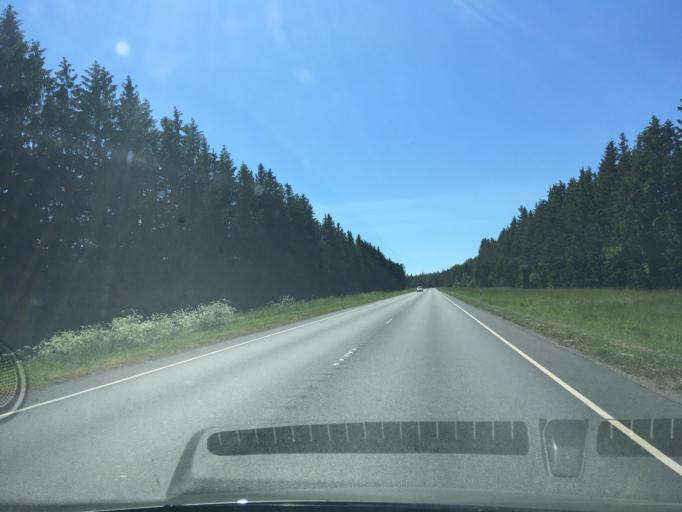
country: EE
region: Laeaene
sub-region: Lihula vald
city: Lihula
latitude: 58.6100
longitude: 23.5795
